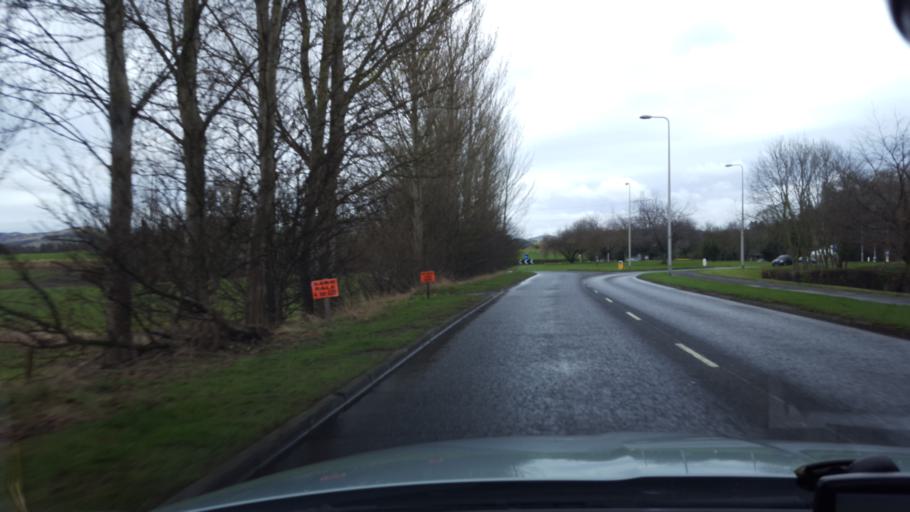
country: GB
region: Scotland
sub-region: Edinburgh
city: Currie
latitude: 55.9136
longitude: -3.3130
